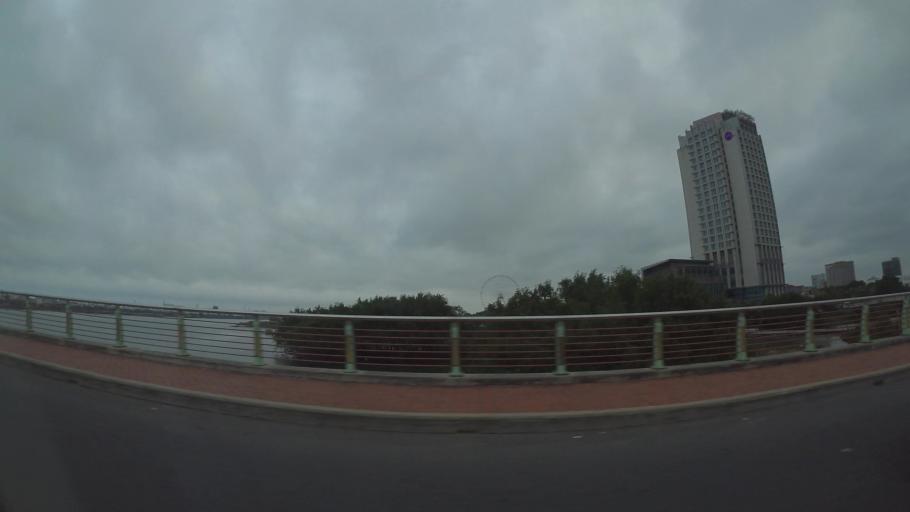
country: VN
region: Da Nang
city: Son Tra
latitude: 16.0500
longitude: 108.2279
